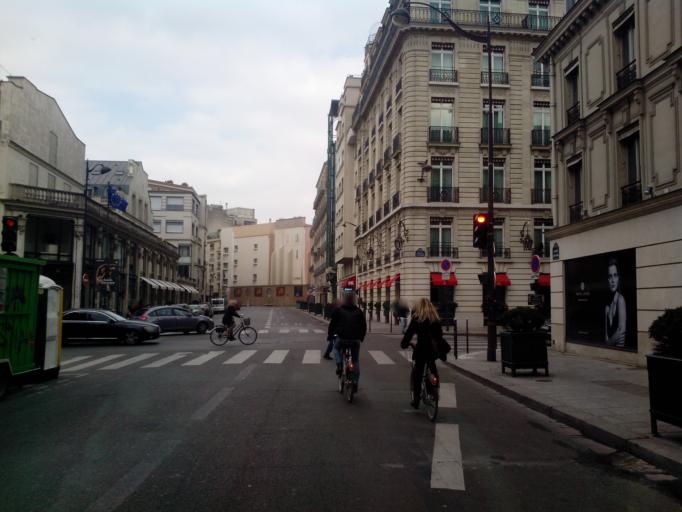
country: FR
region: Ile-de-France
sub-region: Departement des Hauts-de-Seine
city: Clichy
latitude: 48.8716
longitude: 2.3141
